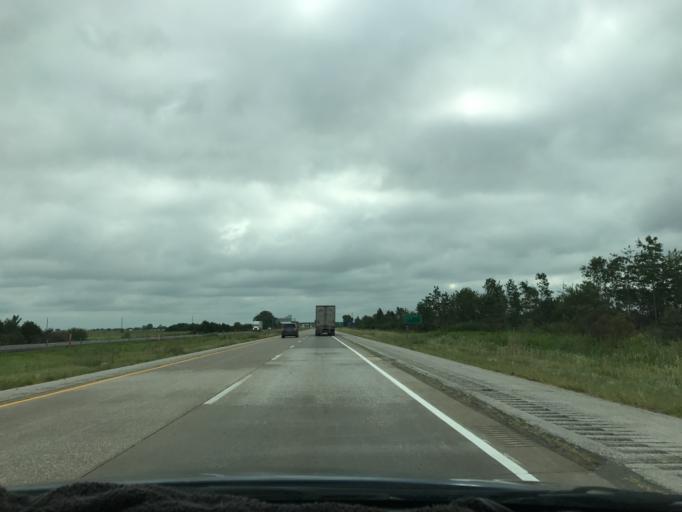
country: US
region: Iowa
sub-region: Scott County
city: Eldridge
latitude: 41.6024
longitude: -90.6555
